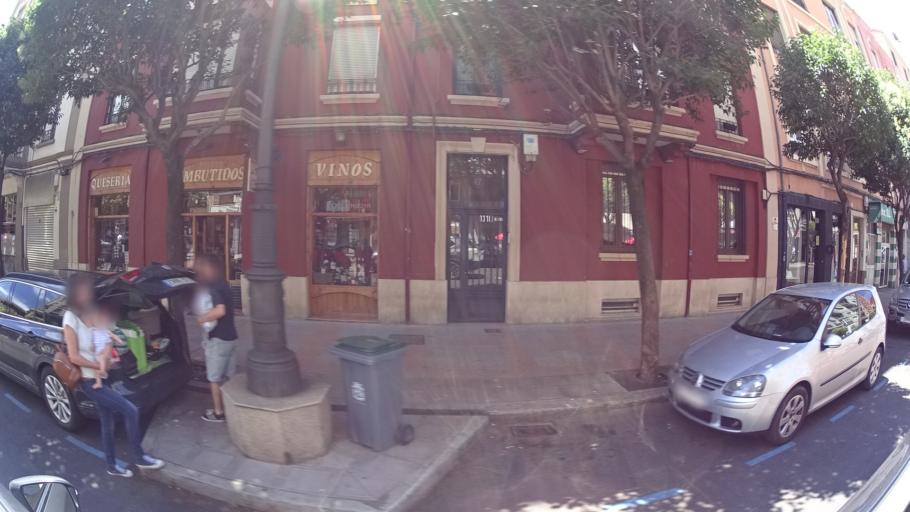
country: ES
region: Castille and Leon
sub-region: Provincia de Leon
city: Leon
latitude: 42.6008
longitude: -5.5791
